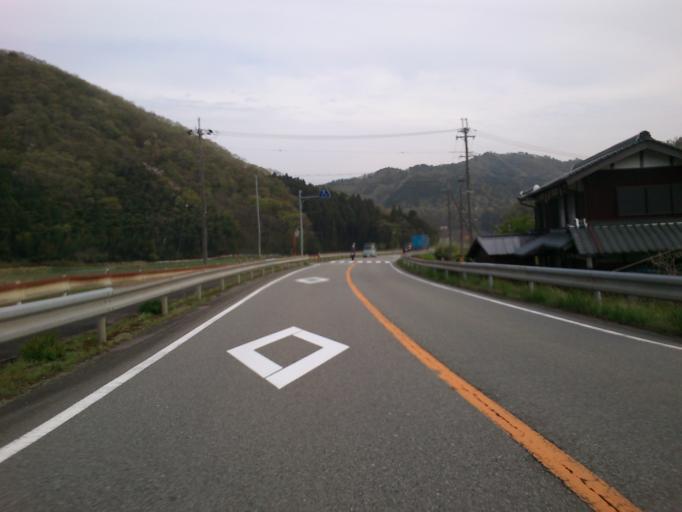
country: JP
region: Hyogo
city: Sasayama
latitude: 35.1251
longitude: 135.3361
